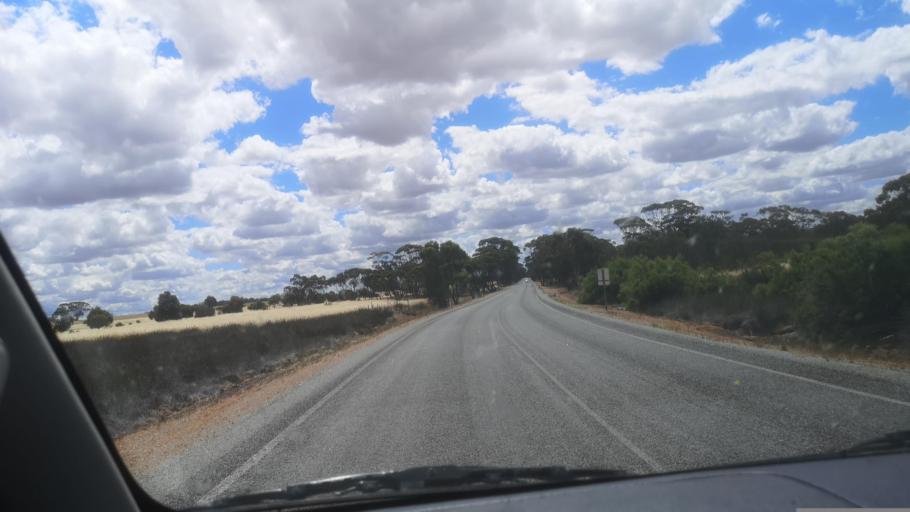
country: AU
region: Western Australia
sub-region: Beverley
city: Beverley
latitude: -31.9968
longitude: 117.1551
